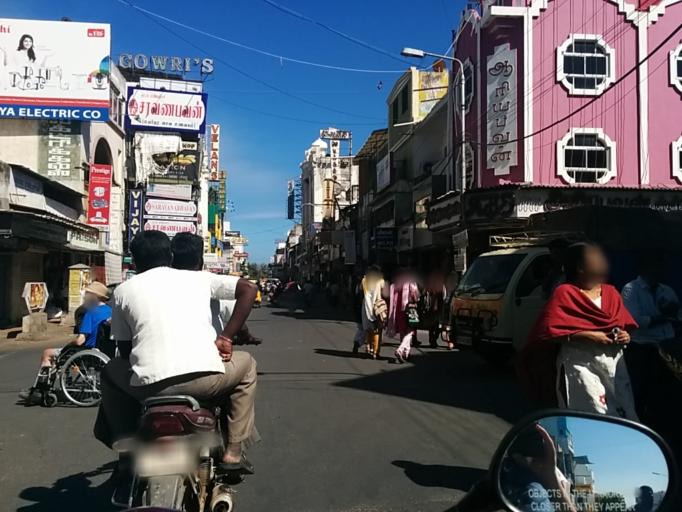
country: IN
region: Pondicherry
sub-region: Puducherry
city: Puducherry
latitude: 11.9362
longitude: 79.8292
